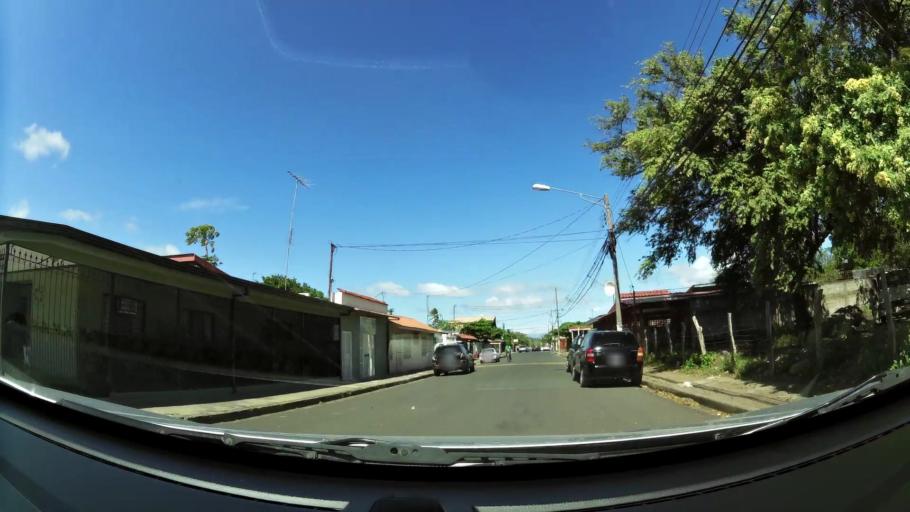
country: CR
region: Guanacaste
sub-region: Canton de Canas
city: Canas
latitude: 10.4293
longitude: -85.0900
